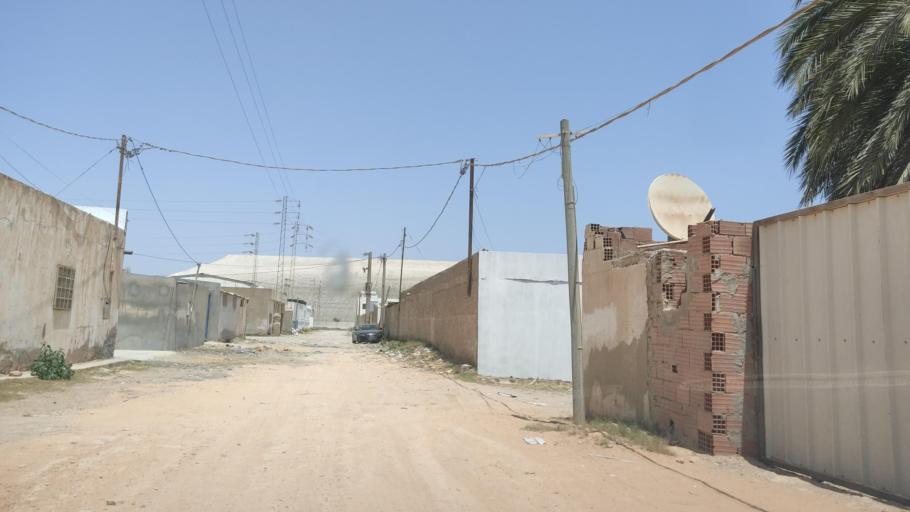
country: TN
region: Safaqis
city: Sfax
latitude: 34.6929
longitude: 10.7236
